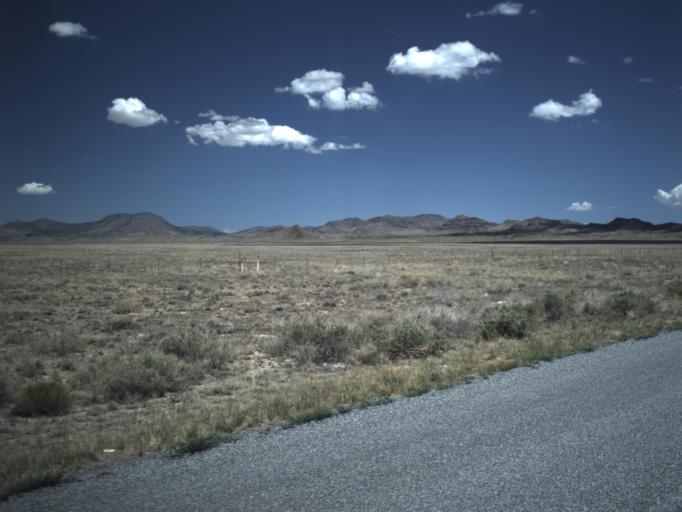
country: US
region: Utah
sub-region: Beaver County
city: Milford
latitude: 39.0583
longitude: -113.7621
